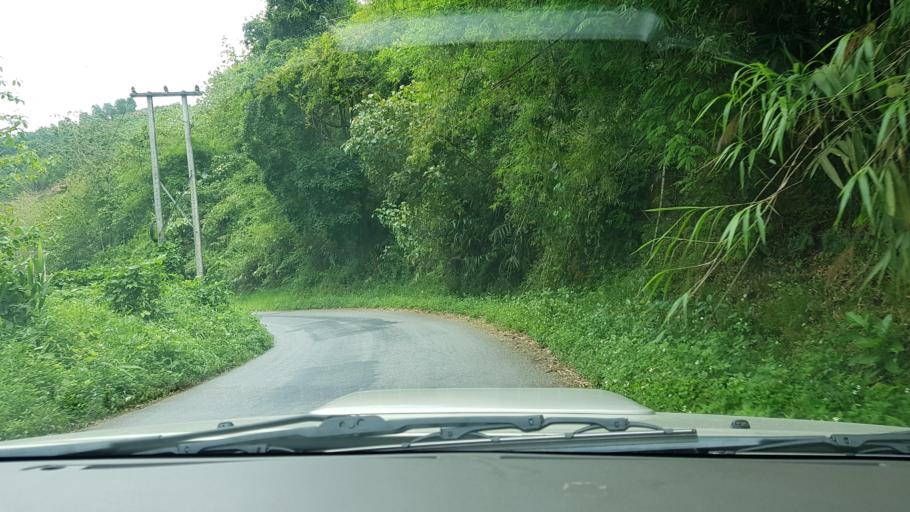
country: LA
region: Phongsali
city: Khoa
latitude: 21.0587
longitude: 102.3883
